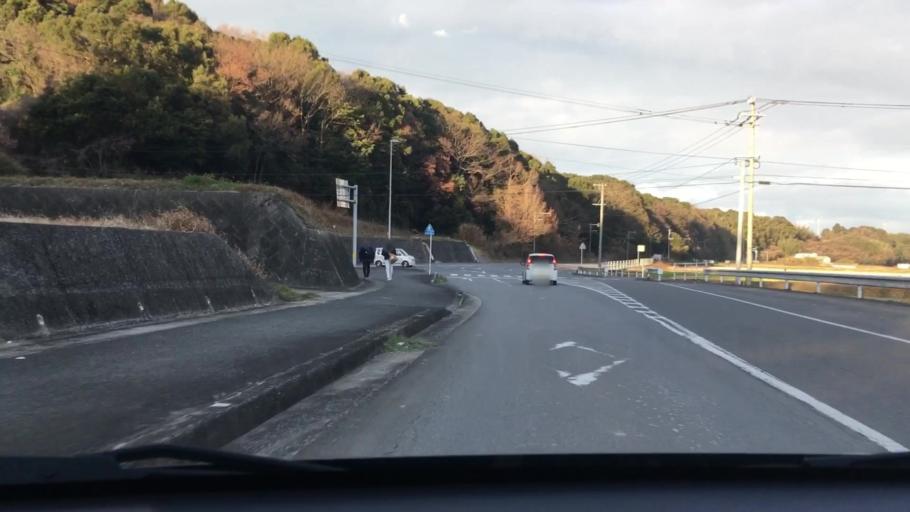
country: JP
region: Oita
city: Bungo-Takada-shi
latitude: 33.5169
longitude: 131.3496
